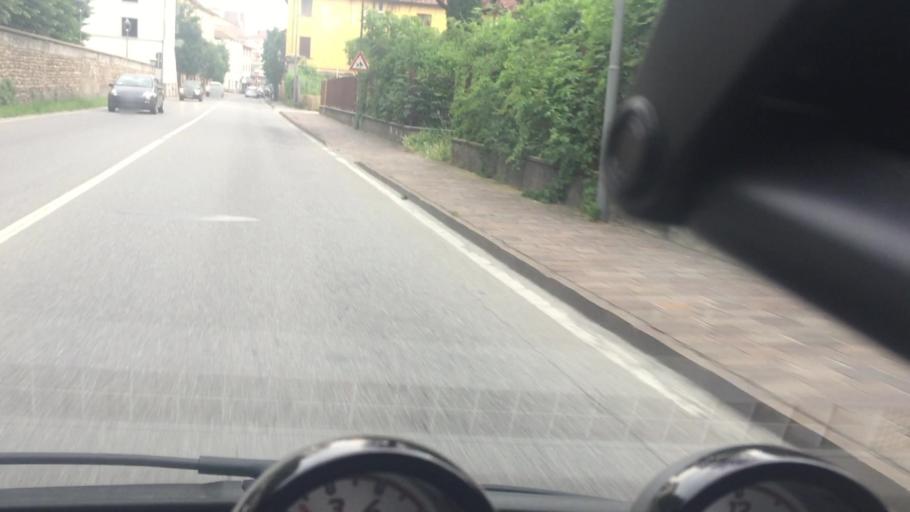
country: IT
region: Lombardy
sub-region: Provincia di Bergamo
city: Boltiere
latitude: 45.6020
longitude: 9.5799
